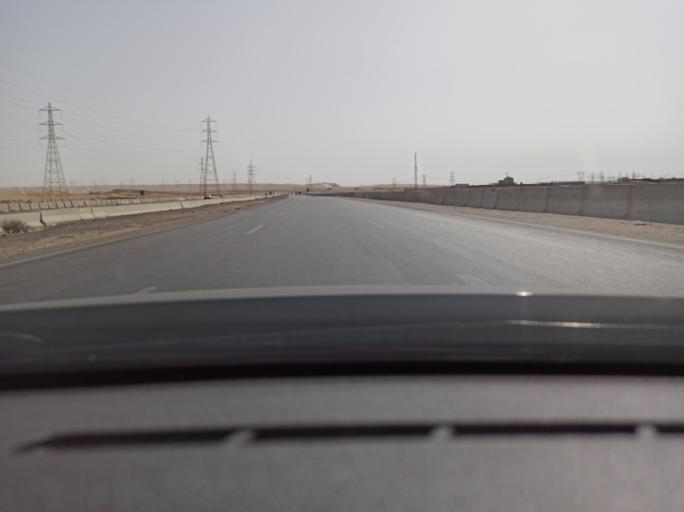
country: EG
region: Muhafazat al Qahirah
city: Halwan
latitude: 29.7671
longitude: 31.3877
